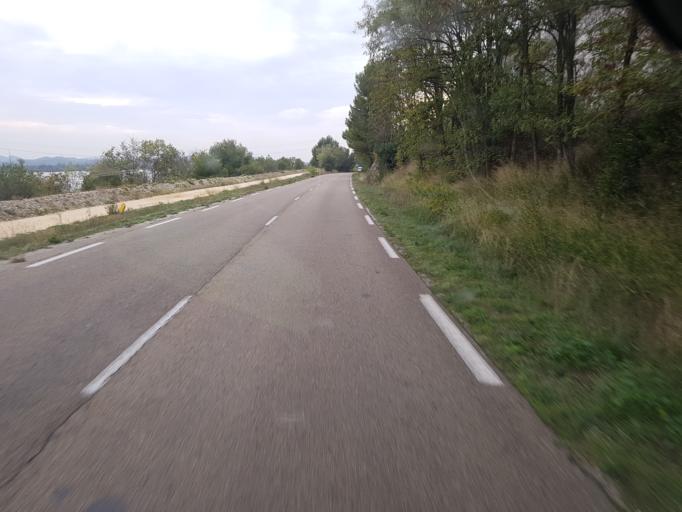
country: FR
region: Provence-Alpes-Cote d'Azur
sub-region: Departement des Bouches-du-Rhone
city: Barbentane
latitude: 43.9303
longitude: 4.7424
